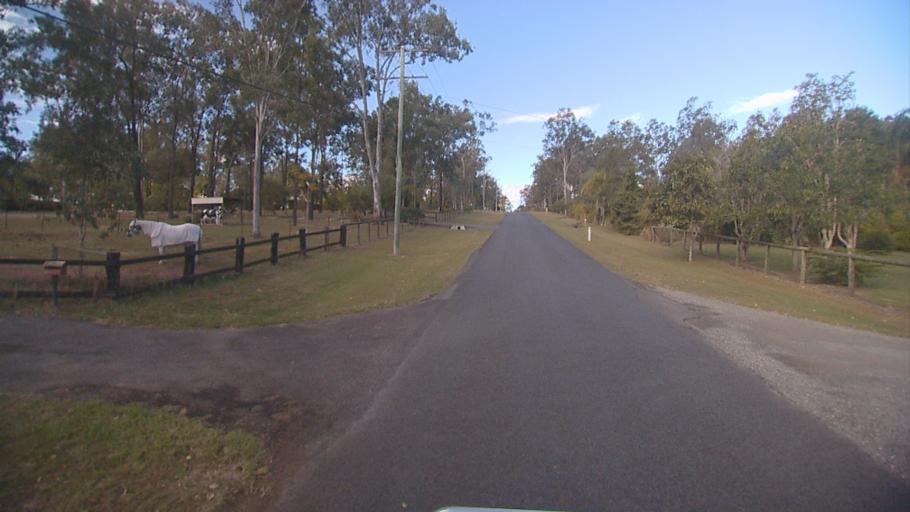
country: AU
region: Queensland
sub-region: Logan
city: North Maclean
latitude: -27.8182
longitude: 153.0506
